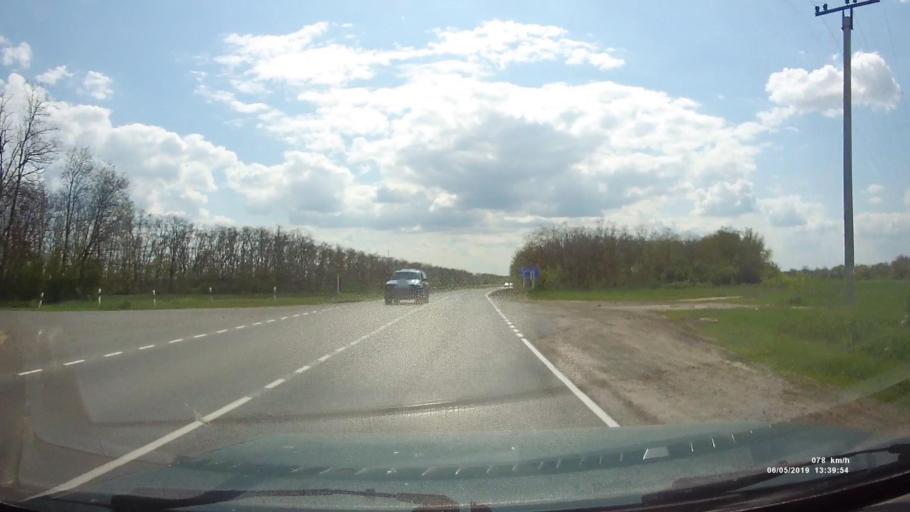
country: RU
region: Rostov
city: Ust'-Donetskiy
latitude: 47.6700
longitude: 40.6998
